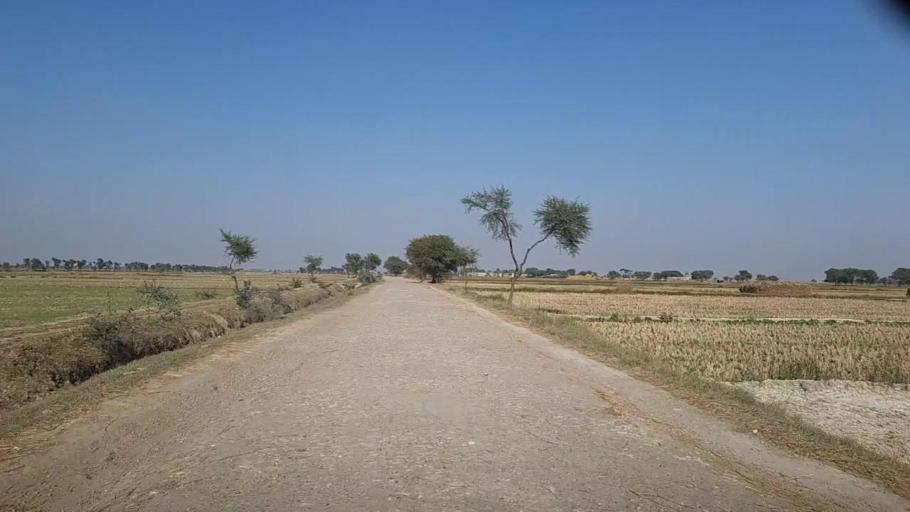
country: PK
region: Sindh
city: Thul
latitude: 28.3506
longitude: 68.7627
